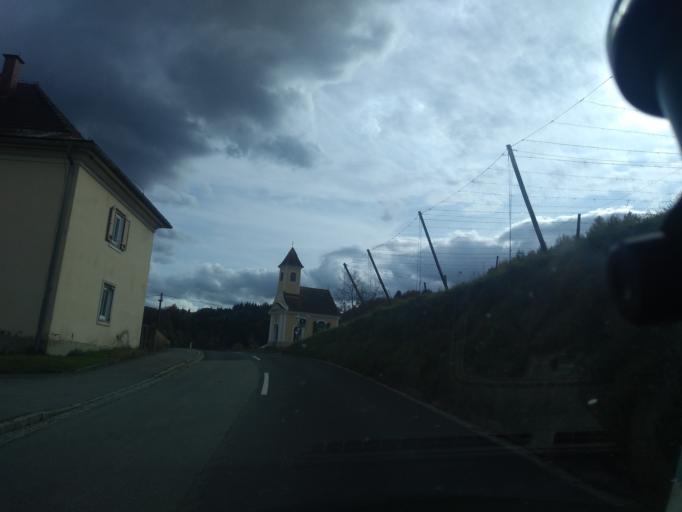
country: AT
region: Styria
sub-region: Politischer Bezirk Leibnitz
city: Leutschach
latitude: 46.6533
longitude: 15.4697
